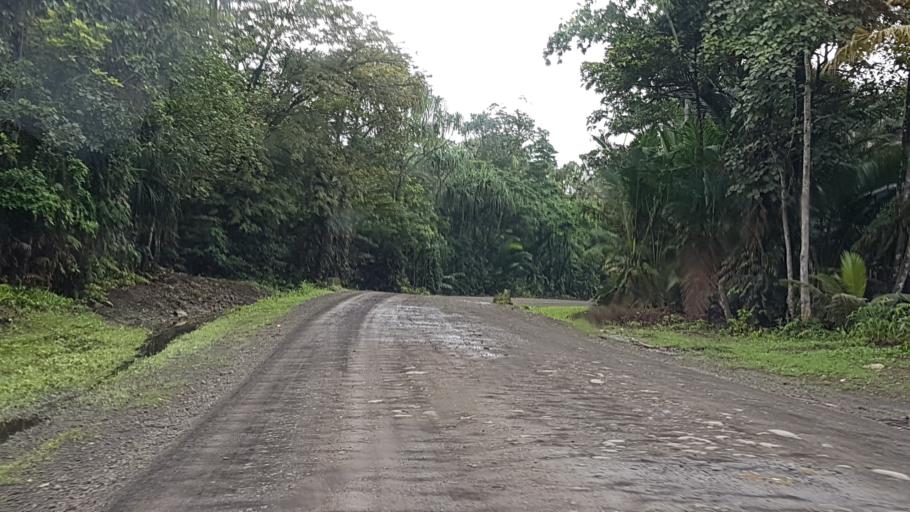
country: PG
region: Milne Bay
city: Alotau
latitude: -10.3333
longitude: 150.5364
